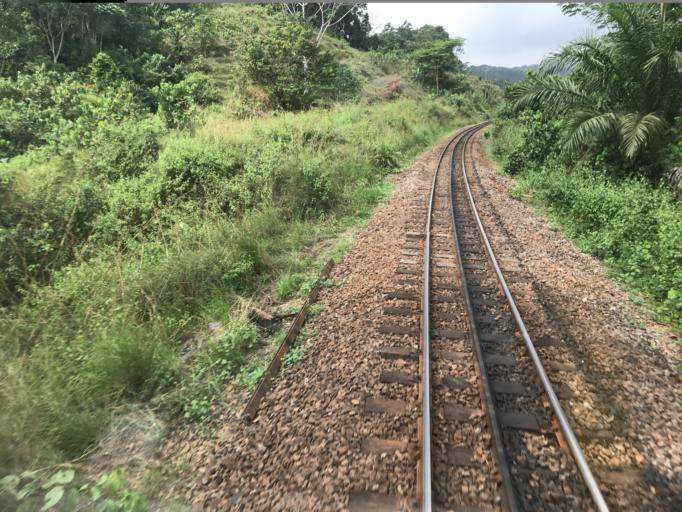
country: CM
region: Centre
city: Eseka
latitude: 3.5867
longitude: 10.8353
